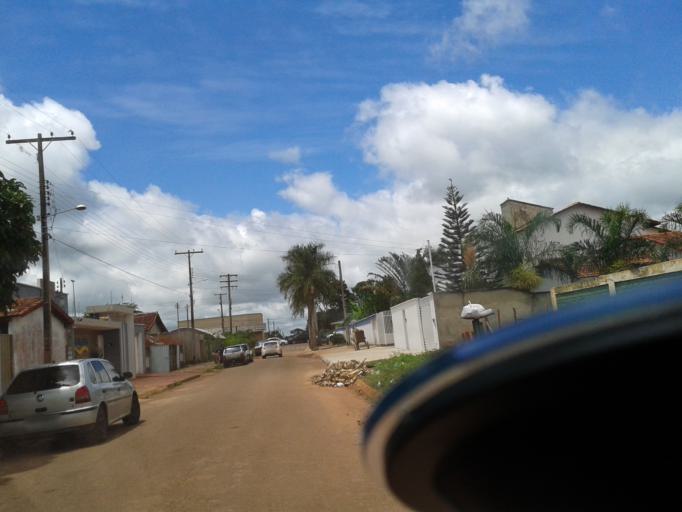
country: BR
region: Goias
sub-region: Itaberai
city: Itaberai
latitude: -16.0381
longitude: -49.7921
